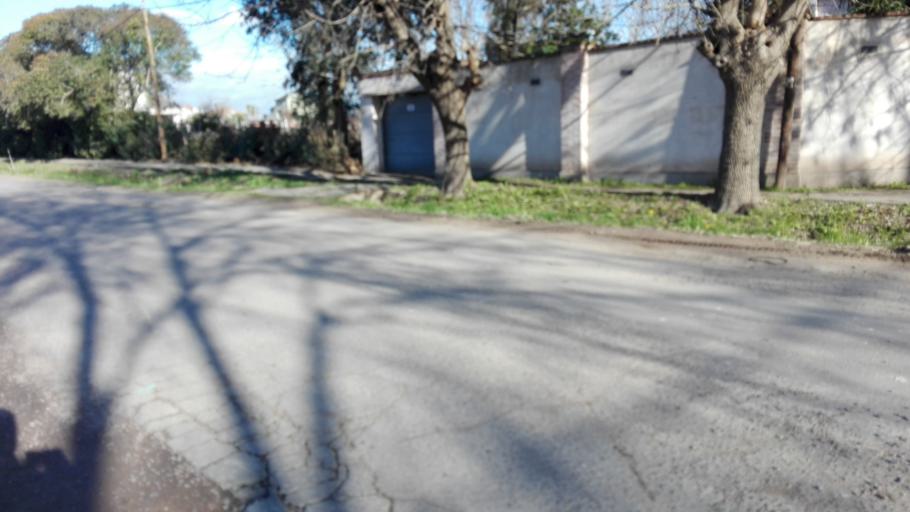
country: AR
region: Buenos Aires
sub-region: Partido de La Plata
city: La Plata
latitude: -34.9056
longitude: -58.0238
